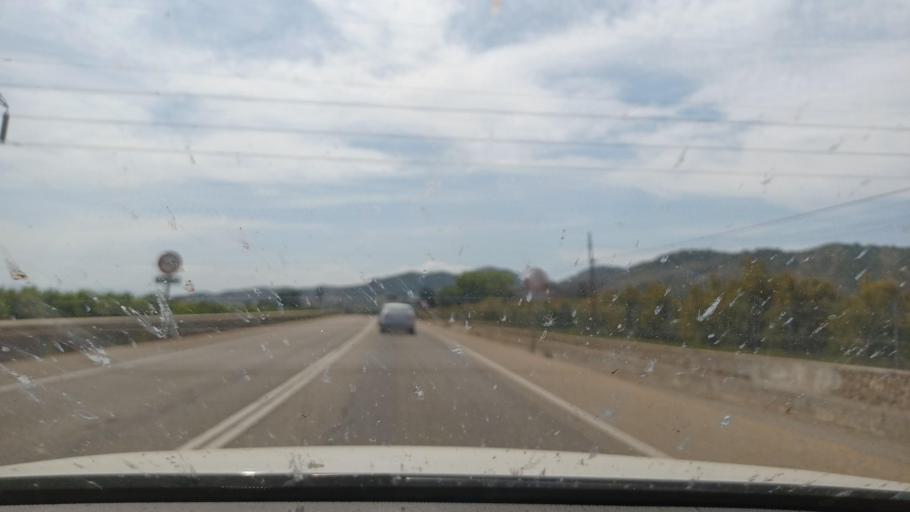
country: ES
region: Valencia
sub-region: Provincia de Castello
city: Castello de la Plana
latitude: 40.0243
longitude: -0.0222
